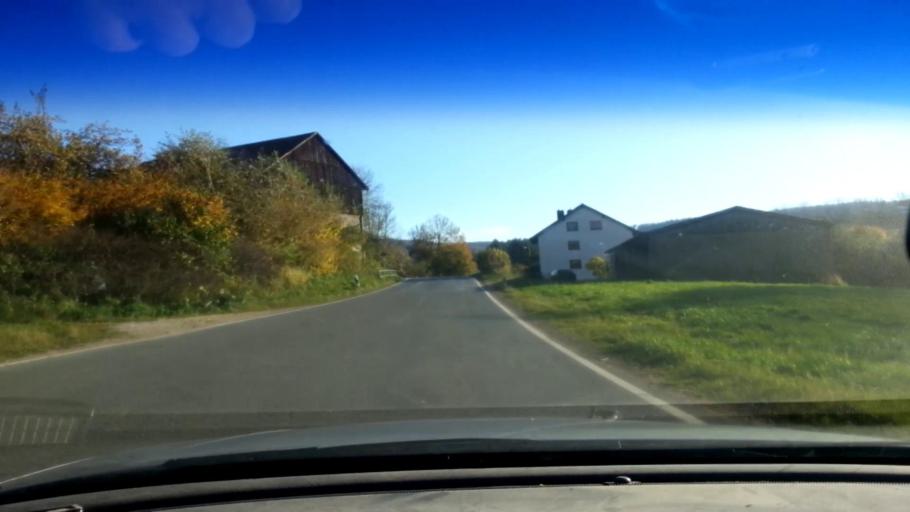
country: DE
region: Bavaria
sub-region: Upper Franconia
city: Heiligenstadt
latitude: 49.8864
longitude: 11.1283
